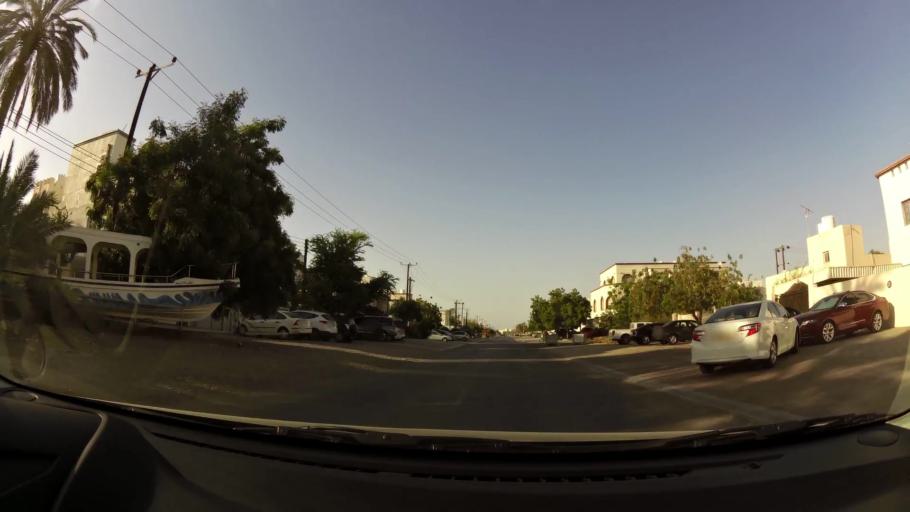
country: OM
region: Muhafazat Masqat
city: As Sib al Jadidah
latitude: 23.6331
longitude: 58.1950
